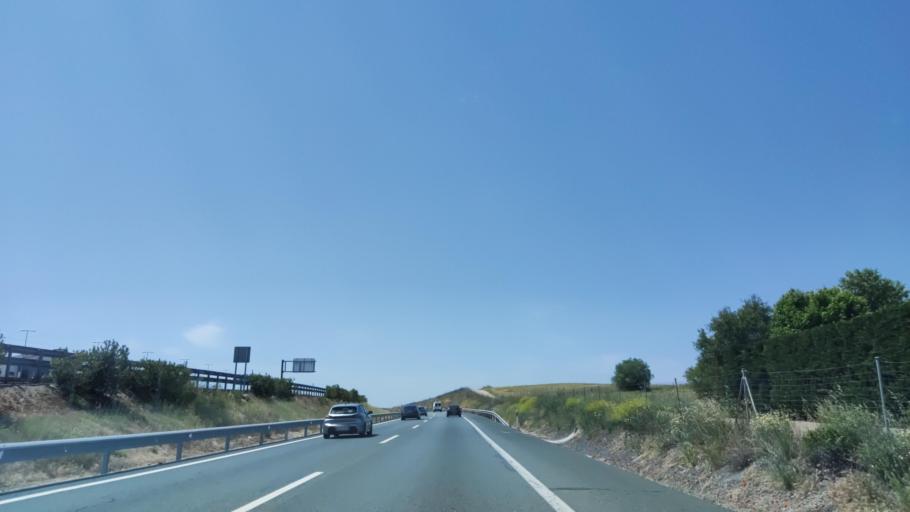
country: ES
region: Castille-La Mancha
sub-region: Province of Toledo
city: Olias del Rey
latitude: 39.9400
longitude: -3.9975
